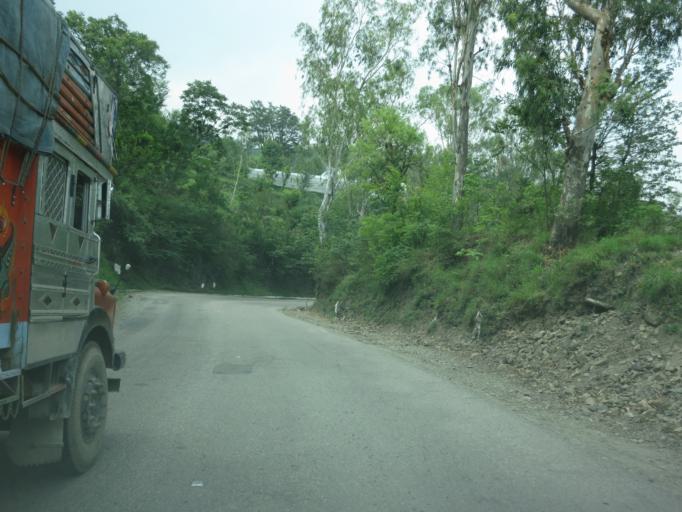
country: IN
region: Himachal Pradesh
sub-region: Bilaspur
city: Bilaspur
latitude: 31.2576
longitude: 76.8661
